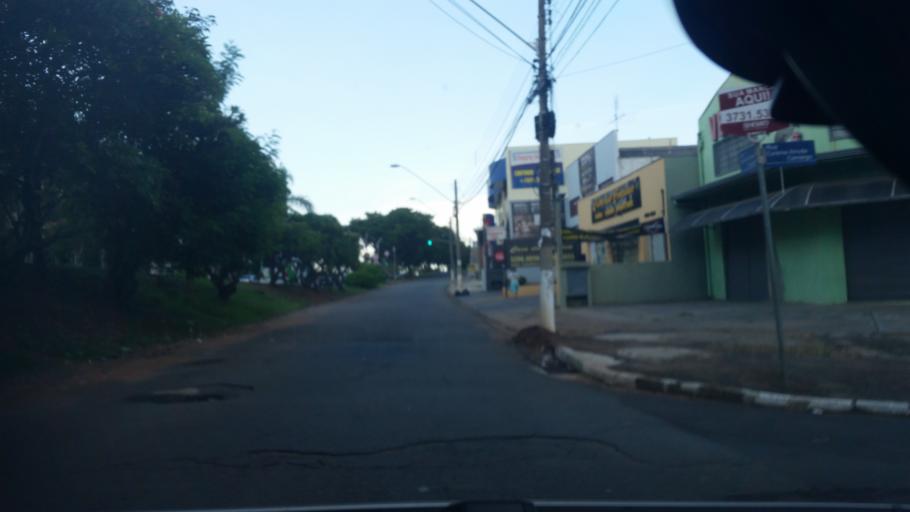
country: BR
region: Sao Paulo
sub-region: Campinas
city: Campinas
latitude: -22.8565
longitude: -47.0440
